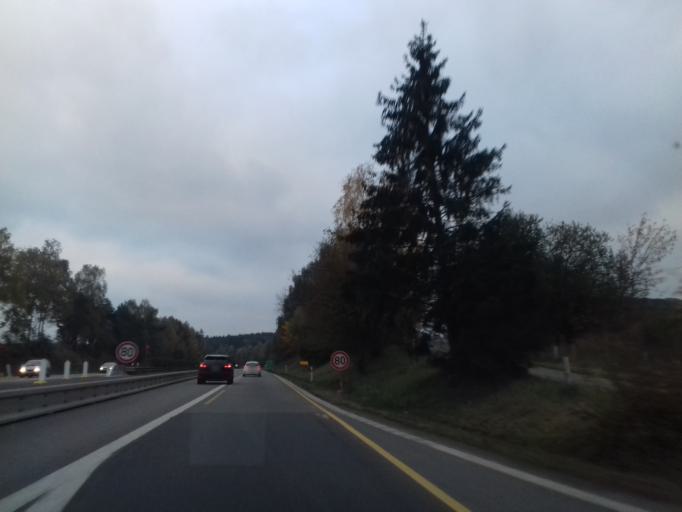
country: CZ
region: Central Bohemia
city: Trhovy Stepanov
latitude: 49.7221
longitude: 15.0496
